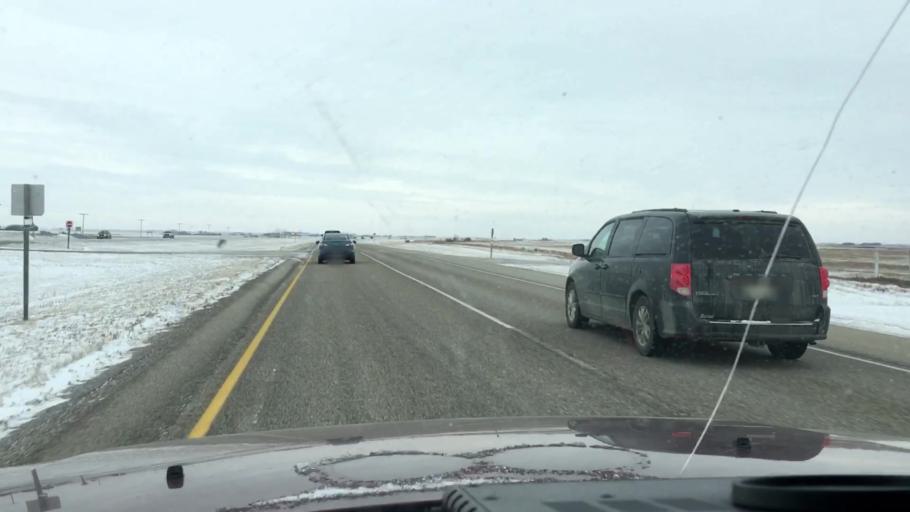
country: CA
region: Saskatchewan
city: Saskatoon
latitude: 51.5922
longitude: -106.3822
